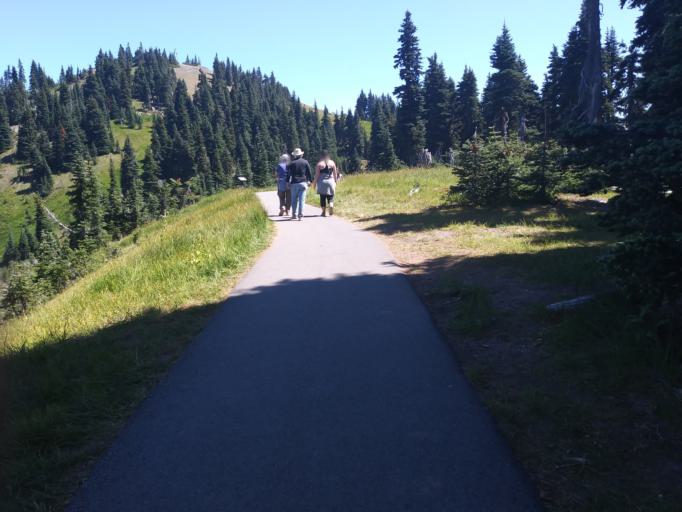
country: US
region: Washington
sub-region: Clallam County
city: Port Angeles
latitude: 47.9712
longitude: -123.4956
